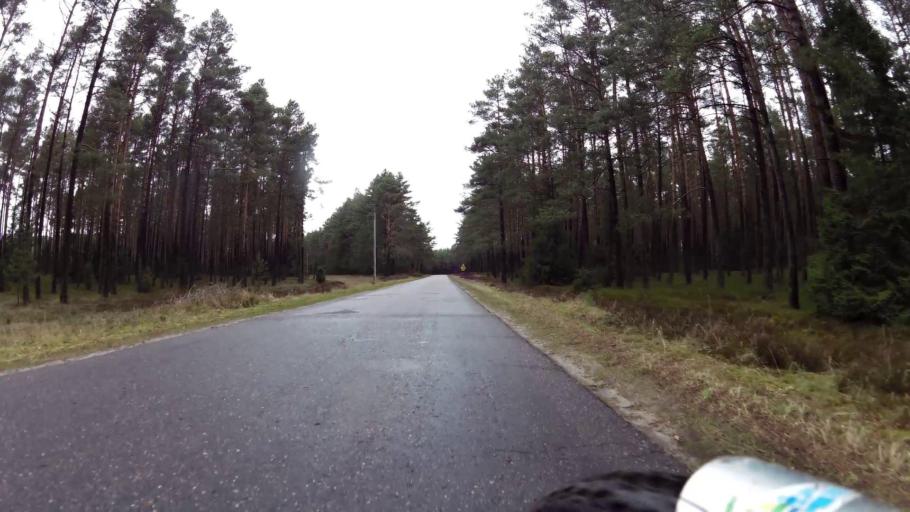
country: PL
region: Pomeranian Voivodeship
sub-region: Powiat bytowski
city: Borzytuchom
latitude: 54.2617
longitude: 17.3665
